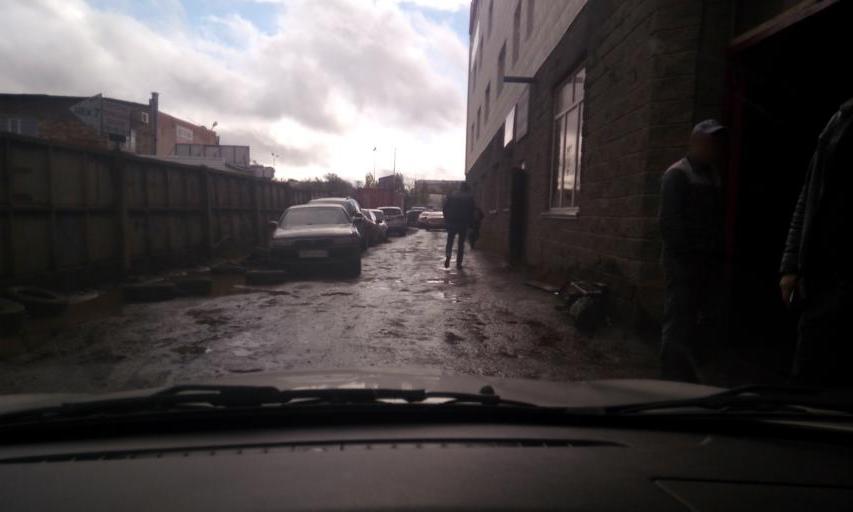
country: KZ
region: Astana Qalasy
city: Astana
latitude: 51.1807
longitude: 71.3815
